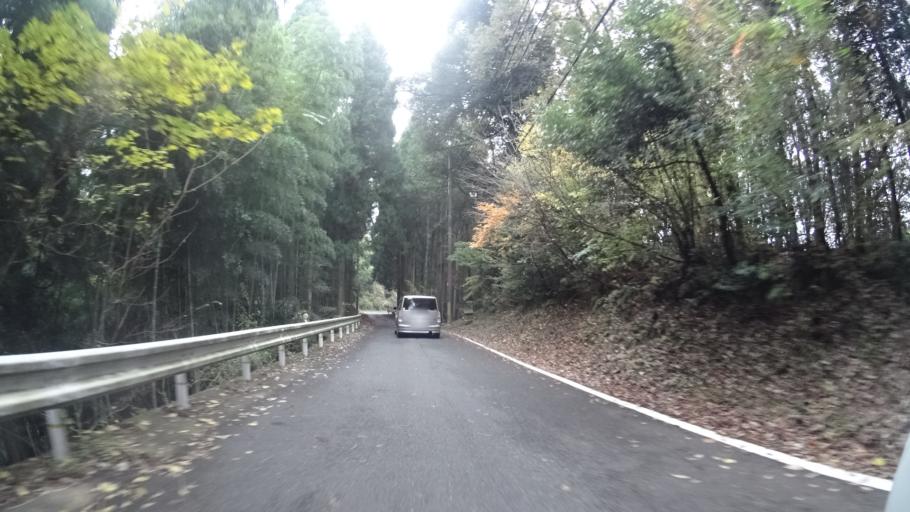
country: JP
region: Kyoto
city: Maizuru
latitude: 35.4923
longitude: 135.4647
